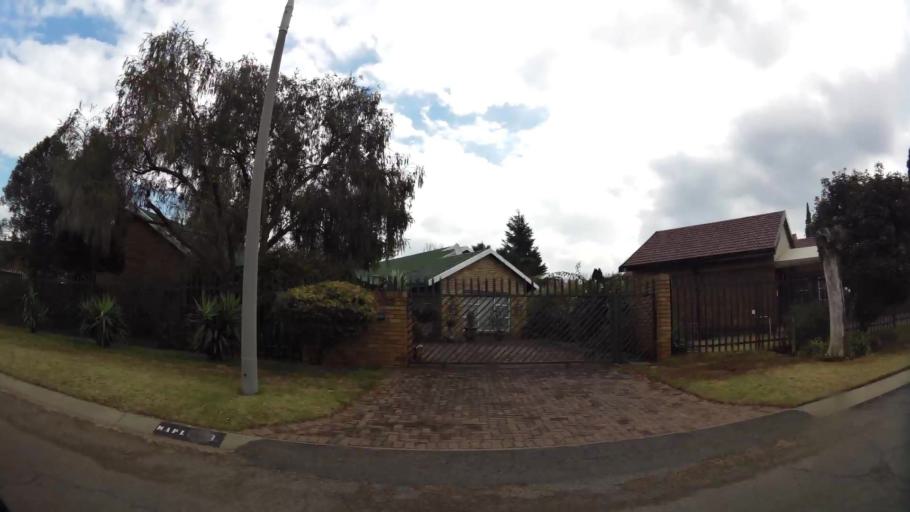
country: ZA
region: Gauteng
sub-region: Sedibeng District Municipality
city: Vanderbijlpark
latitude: -26.7340
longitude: 27.8502
